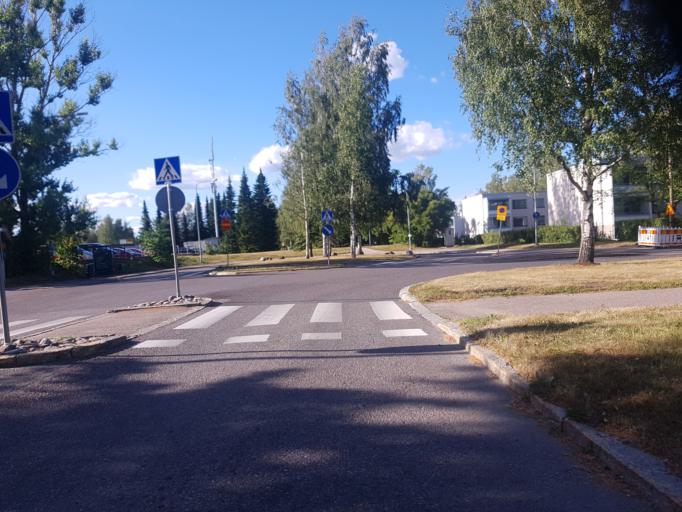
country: FI
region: Uusimaa
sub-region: Helsinki
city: Vantaa
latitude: 60.2770
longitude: 24.9901
